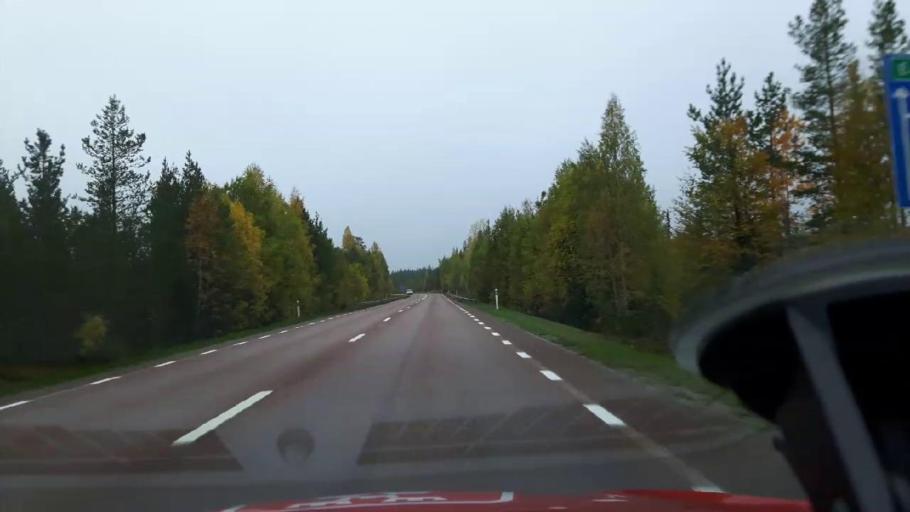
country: SE
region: Jaemtland
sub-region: Bergs Kommun
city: Hoverberg
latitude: 62.6243
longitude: 14.3718
